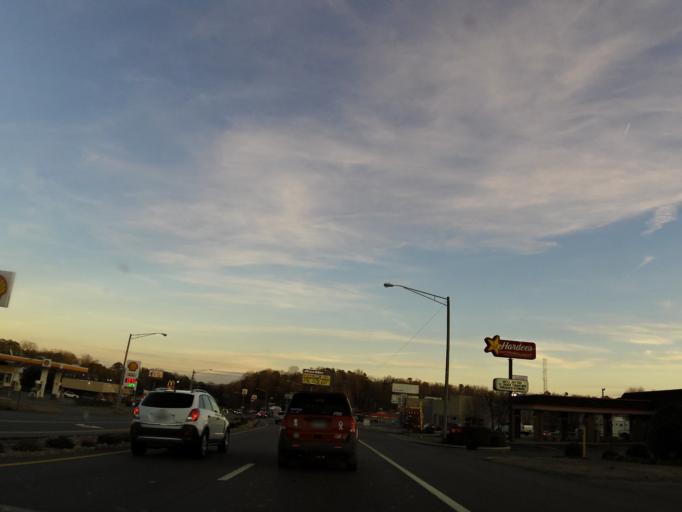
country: US
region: Tennessee
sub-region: Bradley County
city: Cleveland
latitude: 35.1912
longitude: -84.8844
